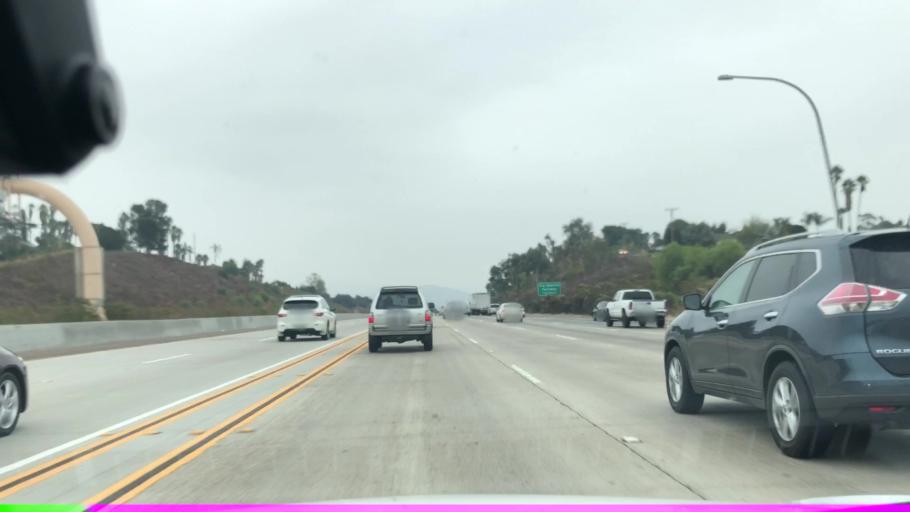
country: US
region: California
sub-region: San Diego County
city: Escondido
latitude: 33.0895
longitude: -117.0796
